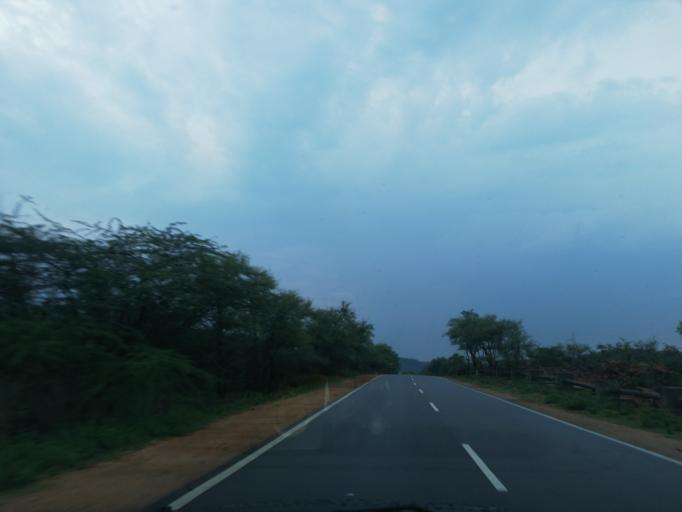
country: IN
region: Andhra Pradesh
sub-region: Guntur
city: Macherla
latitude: 16.6494
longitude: 79.2893
